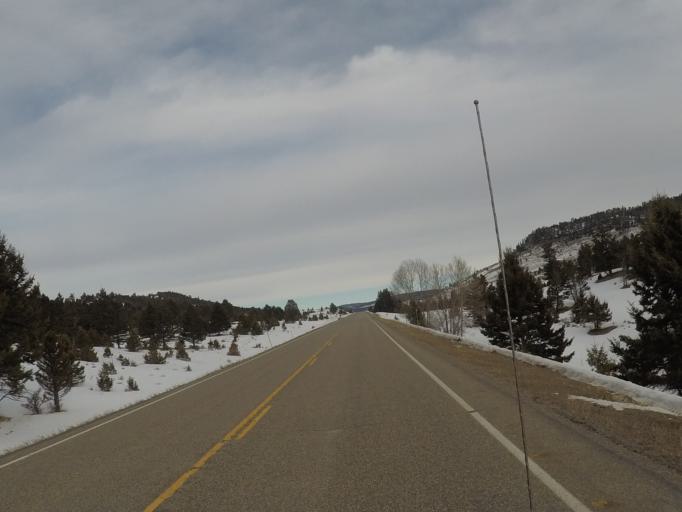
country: US
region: Montana
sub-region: Meagher County
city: White Sulphur Springs
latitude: 46.6373
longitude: -110.8574
